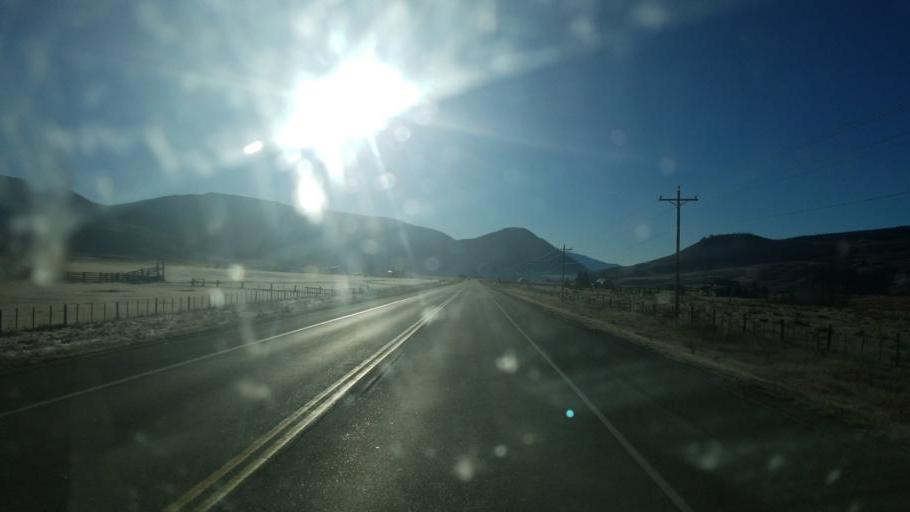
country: US
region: Colorado
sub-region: Gunnison County
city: Crested Butte
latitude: 38.8403
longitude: -106.9395
